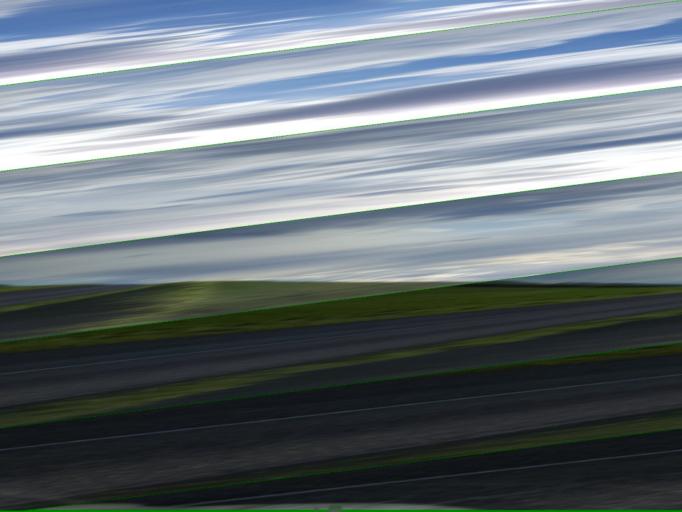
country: FR
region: Ile-de-France
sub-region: Departement du Val-d'Oise
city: Magny-en-Vexin
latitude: 49.1869
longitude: 1.8288
